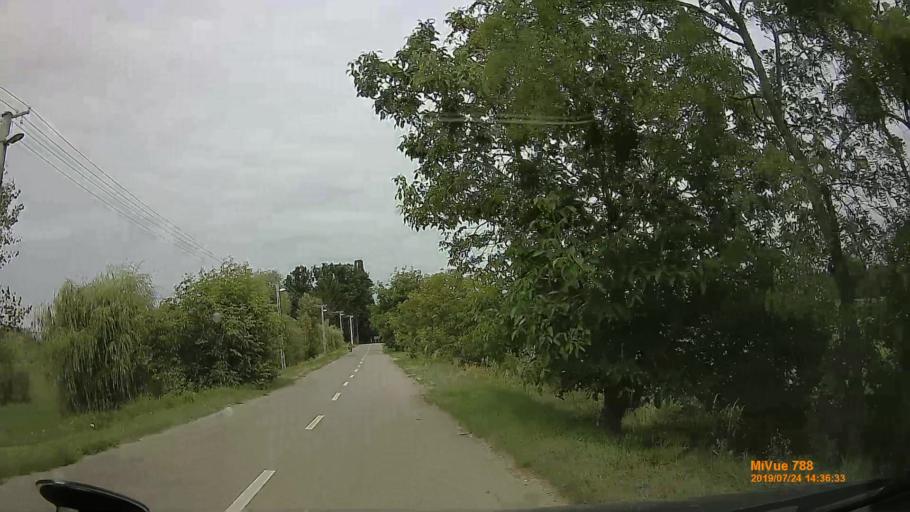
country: HU
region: Szabolcs-Szatmar-Bereg
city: Mandok
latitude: 48.3220
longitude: 22.2643
